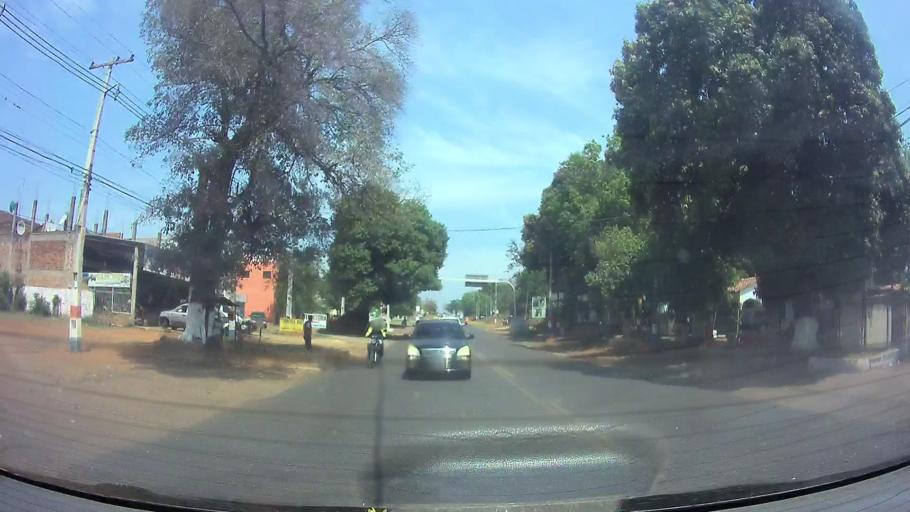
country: PY
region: Central
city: Capiata
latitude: -25.3946
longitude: -57.4675
